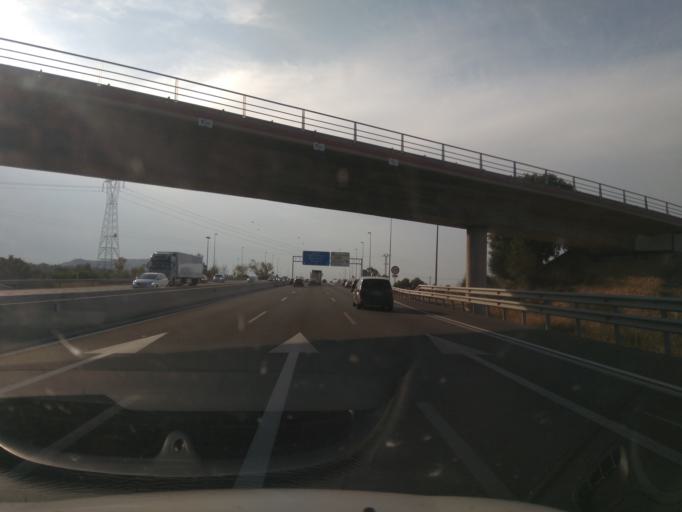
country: ES
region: Valencia
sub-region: Provincia de Valencia
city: Torrent
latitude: 39.4150
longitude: -0.5054
